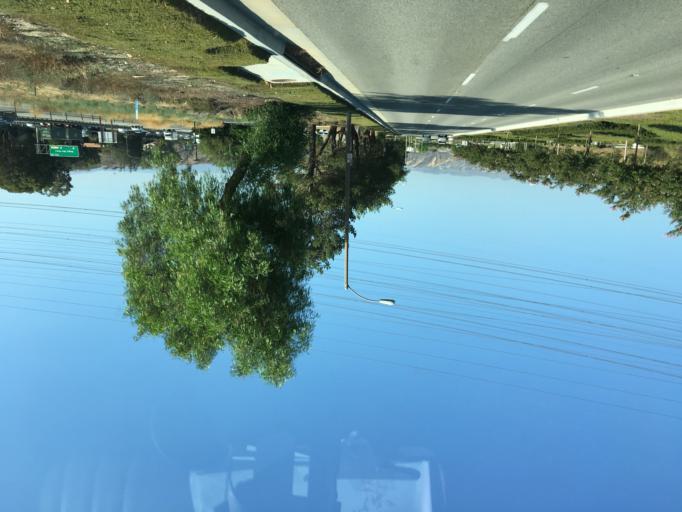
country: US
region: California
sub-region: Los Angeles County
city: Valencia
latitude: 34.4176
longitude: -118.5811
